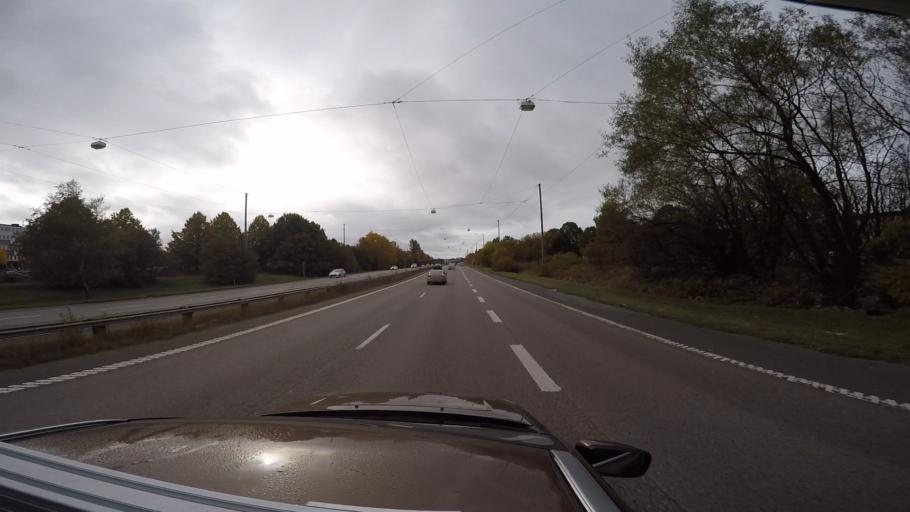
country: SE
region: Vaestra Goetaland
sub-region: Goteborg
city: Majorna
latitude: 57.6666
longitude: 11.9372
